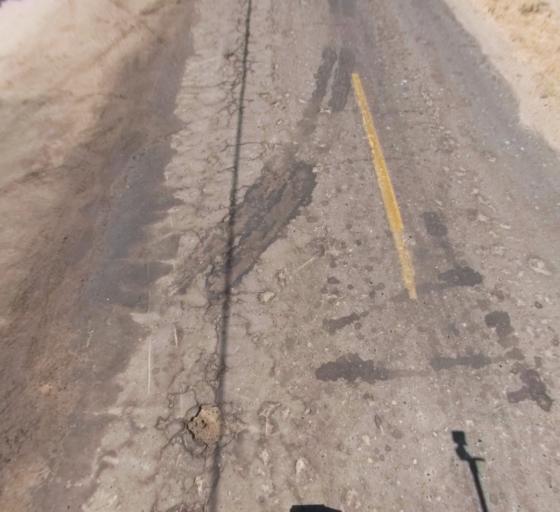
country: US
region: California
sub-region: Fresno County
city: Biola
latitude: 36.8631
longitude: -120.0103
